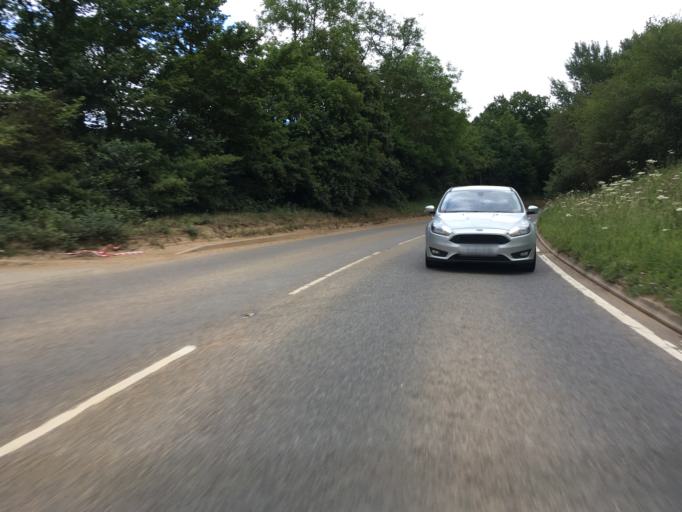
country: GB
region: England
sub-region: Central Bedfordshire
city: Potsgrove
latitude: 51.9529
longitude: -0.6525
